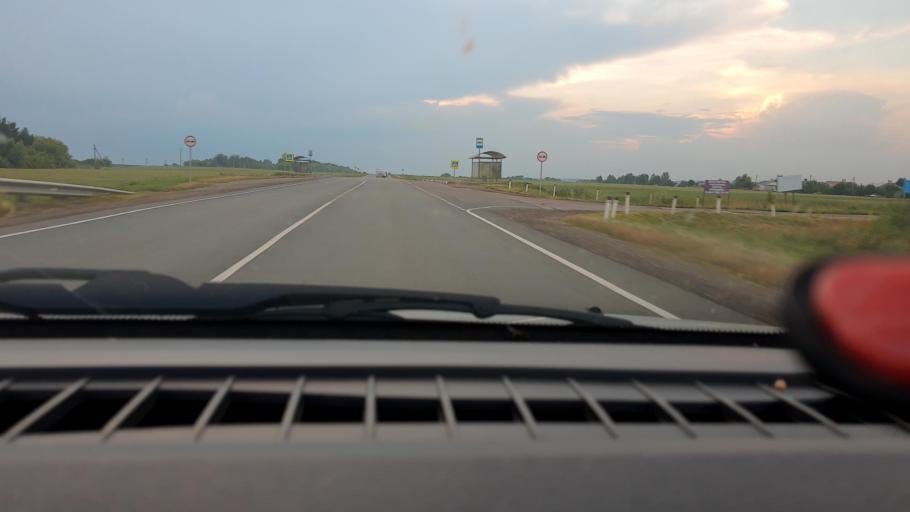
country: RU
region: Nizjnij Novgorod
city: Shatki
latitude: 55.2582
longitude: 43.9788
